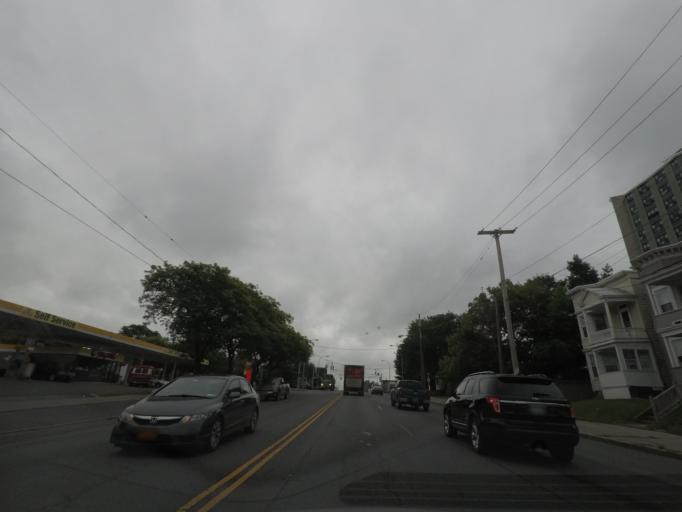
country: US
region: New York
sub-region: Albany County
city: West Albany
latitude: 42.6753
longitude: -73.7846
